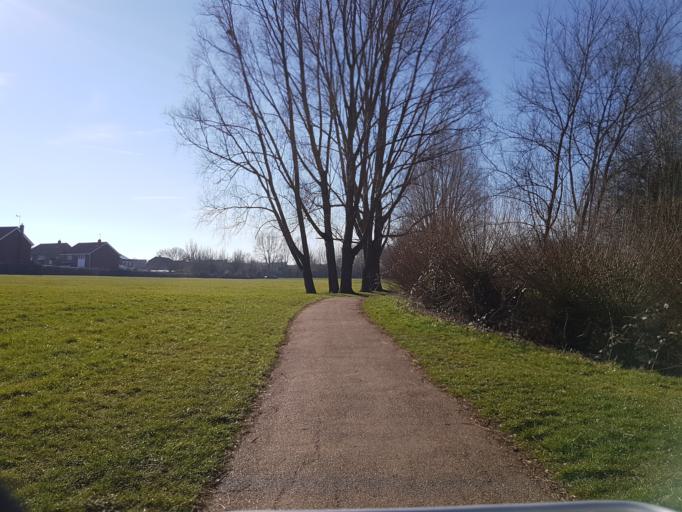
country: GB
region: England
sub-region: Milton Keynes
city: Shenley Church End
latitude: 52.0093
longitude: -0.7628
